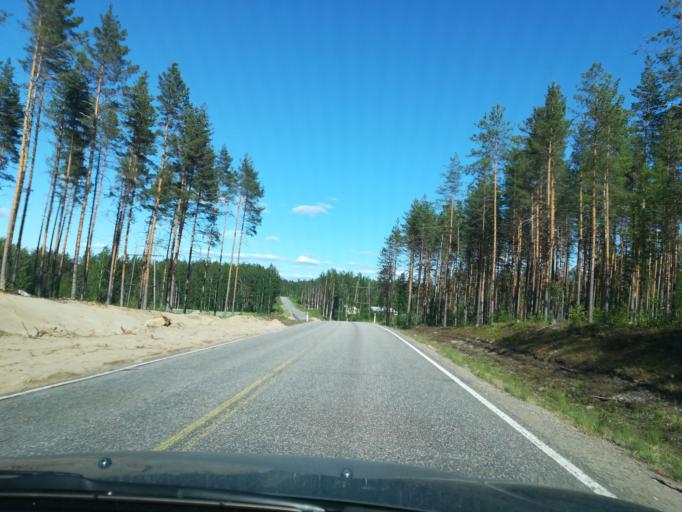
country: FI
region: Southern Savonia
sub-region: Mikkeli
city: Puumala
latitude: 61.4641
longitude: 28.3448
